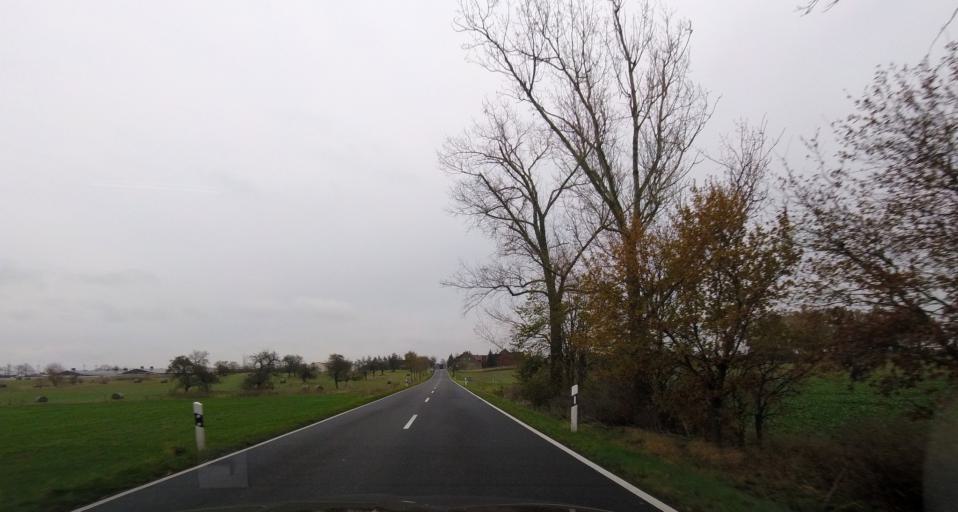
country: DE
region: Saxony-Anhalt
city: Kropstadt
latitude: 52.0048
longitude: 12.7698
